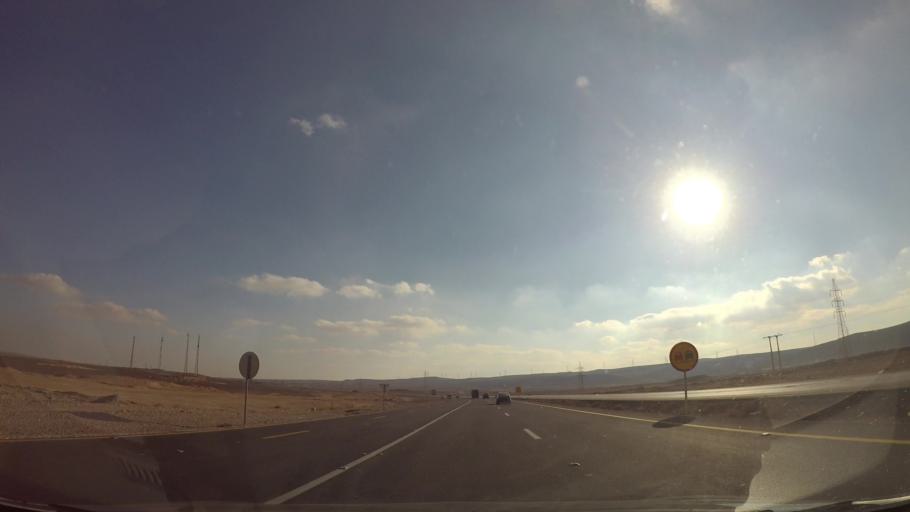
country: JO
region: Karak
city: Karak City
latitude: 31.1162
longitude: 36.0085
